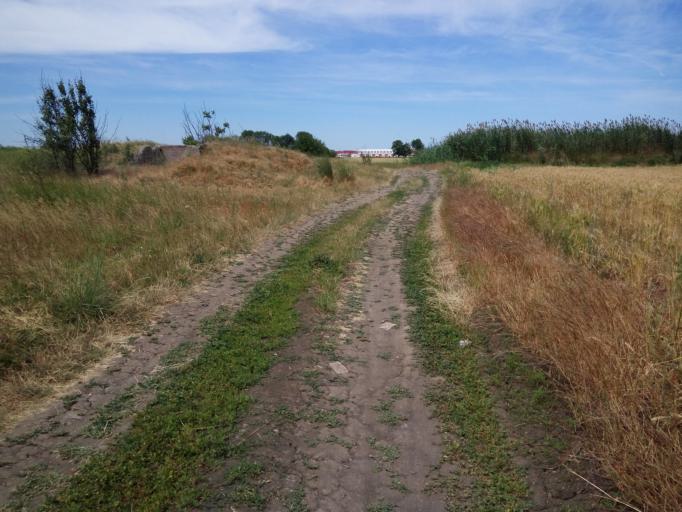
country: RU
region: Rostov
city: Bataysk
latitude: 47.1209
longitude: 39.7225
